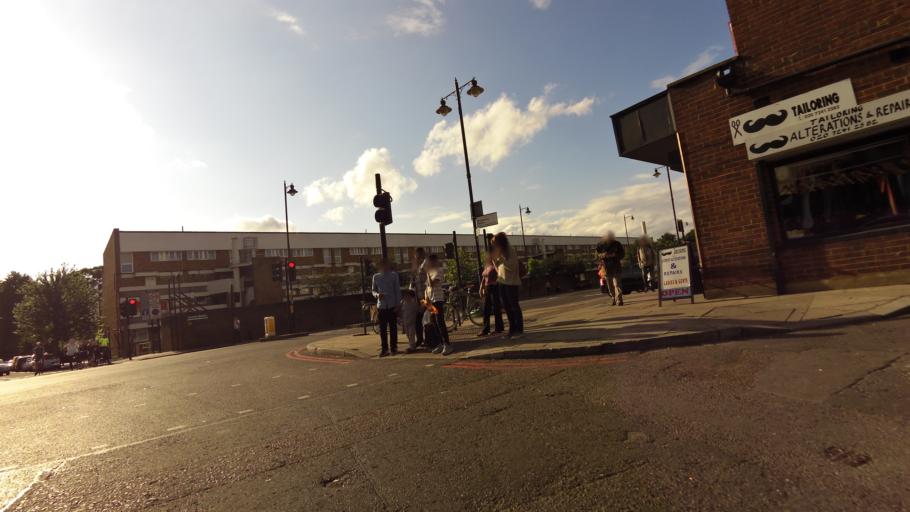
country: GB
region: England
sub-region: Greater London
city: Bethnal Green
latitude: 51.5408
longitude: -0.0762
